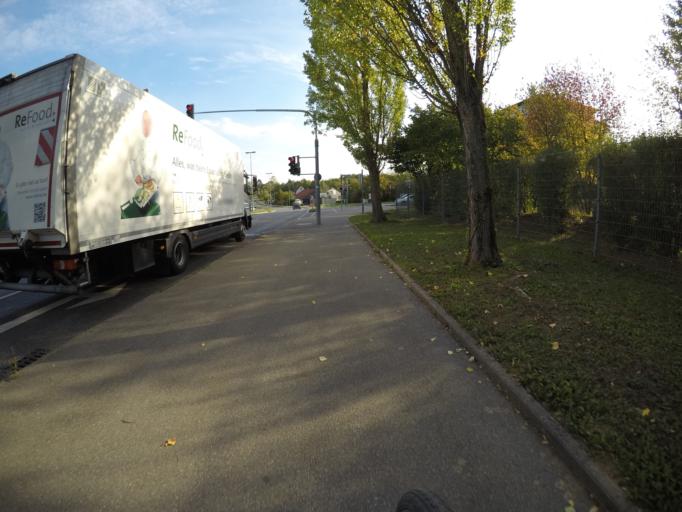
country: DE
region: Baden-Wuerttemberg
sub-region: Tuebingen Region
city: Sickenhausen
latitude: 48.5172
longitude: 9.2009
